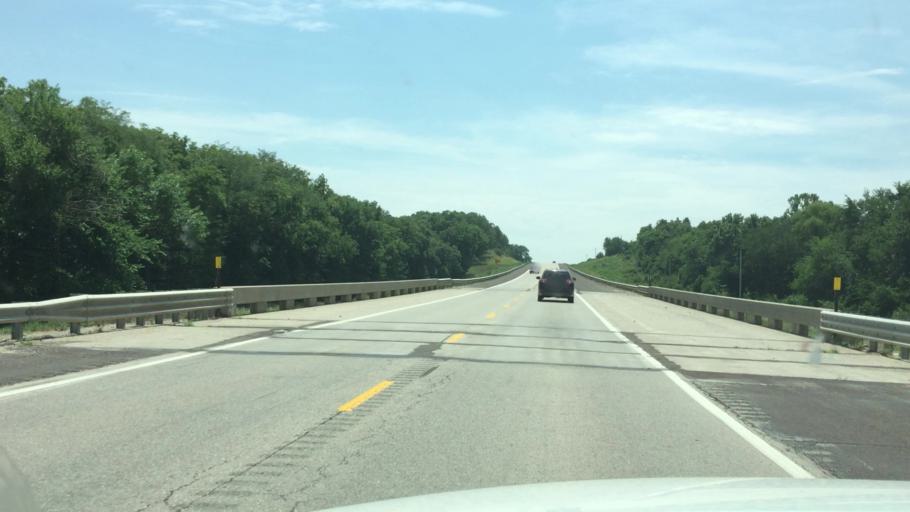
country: US
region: Kansas
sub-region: Jackson County
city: Holton
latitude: 39.5463
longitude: -95.7483
